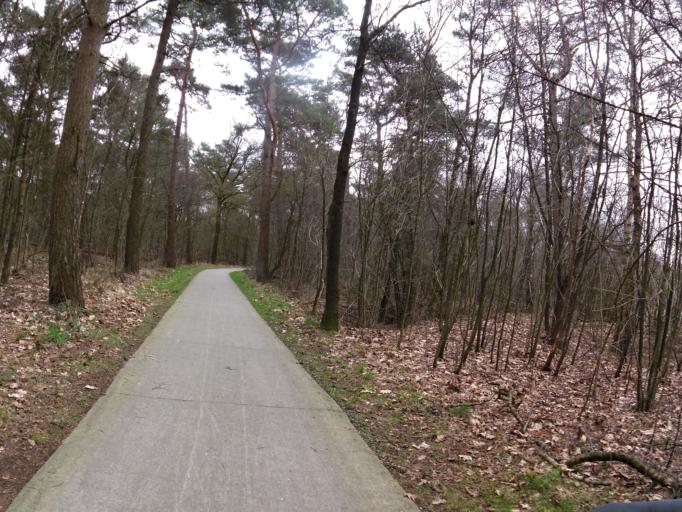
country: NL
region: Drenthe
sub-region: Gemeente Westerveld
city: Dwingeloo
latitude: 52.9239
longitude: 6.2819
